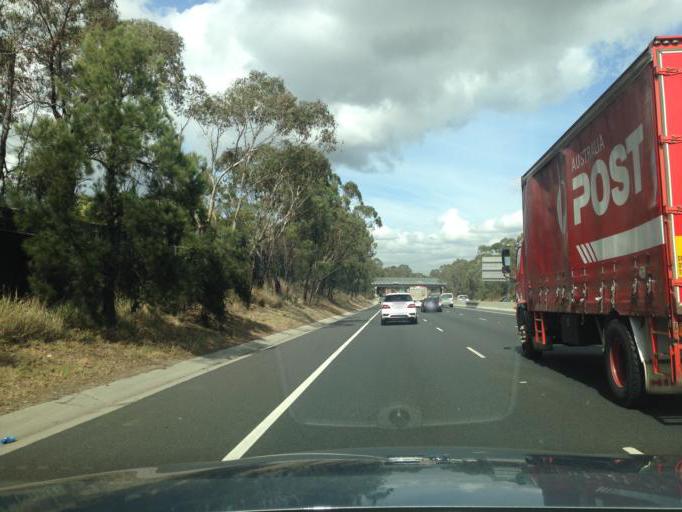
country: AU
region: New South Wales
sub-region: Bankstown
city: Revesby
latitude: -33.9408
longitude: 151.0045
